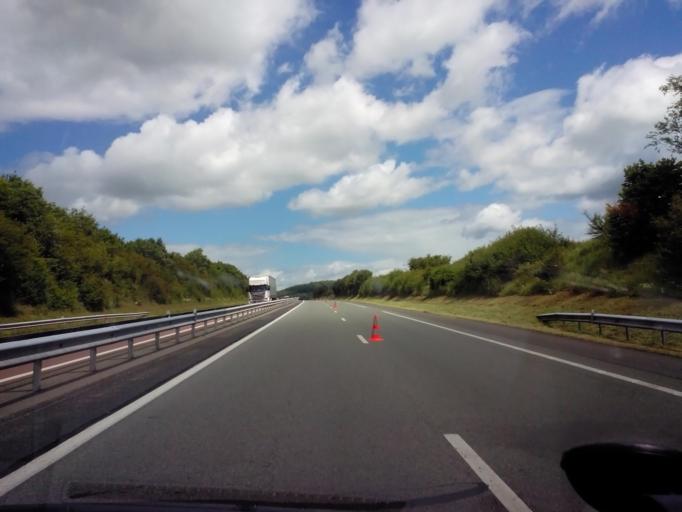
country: FR
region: Champagne-Ardenne
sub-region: Departement de la Haute-Marne
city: Avrecourt
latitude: 48.0446
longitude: 5.5697
